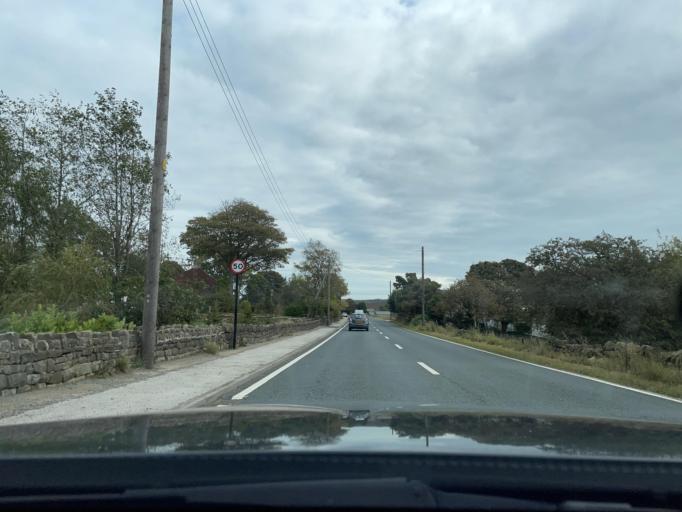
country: GB
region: England
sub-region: Sheffield
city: Bradfield
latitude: 53.3881
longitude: -1.6337
